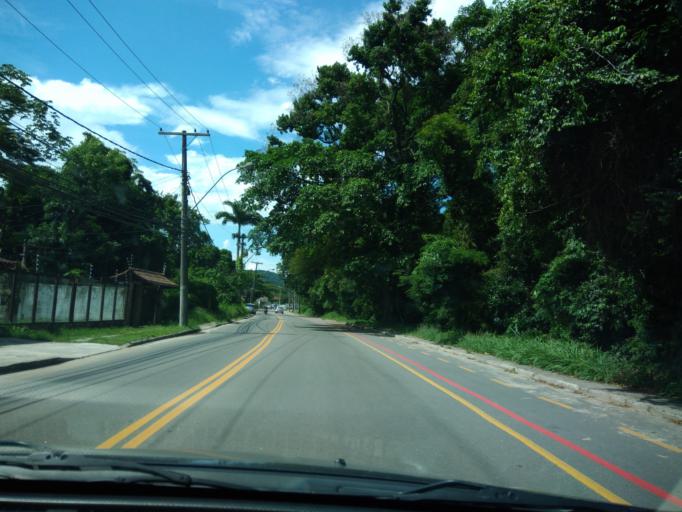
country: BR
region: Rio de Janeiro
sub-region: Niteroi
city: Niteroi
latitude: -22.9486
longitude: -43.0240
